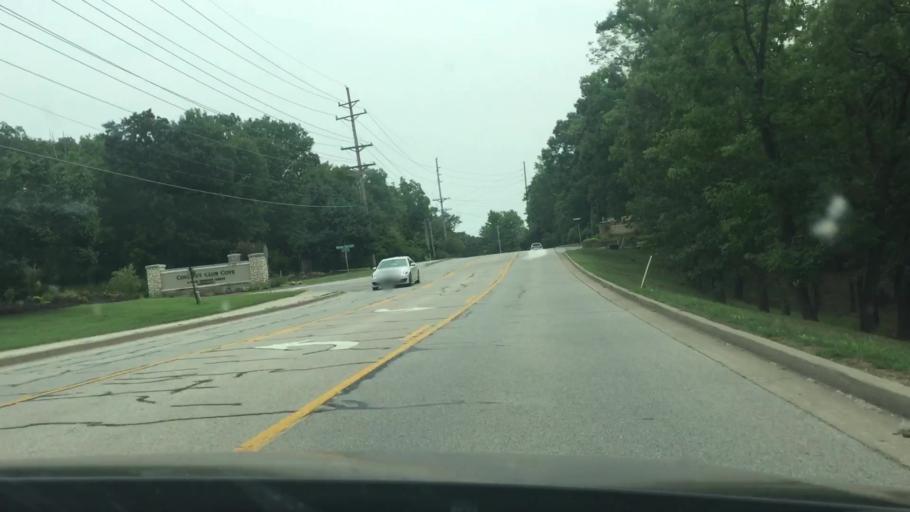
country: US
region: Missouri
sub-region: Camden County
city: Four Seasons
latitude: 38.1908
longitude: -92.6984
